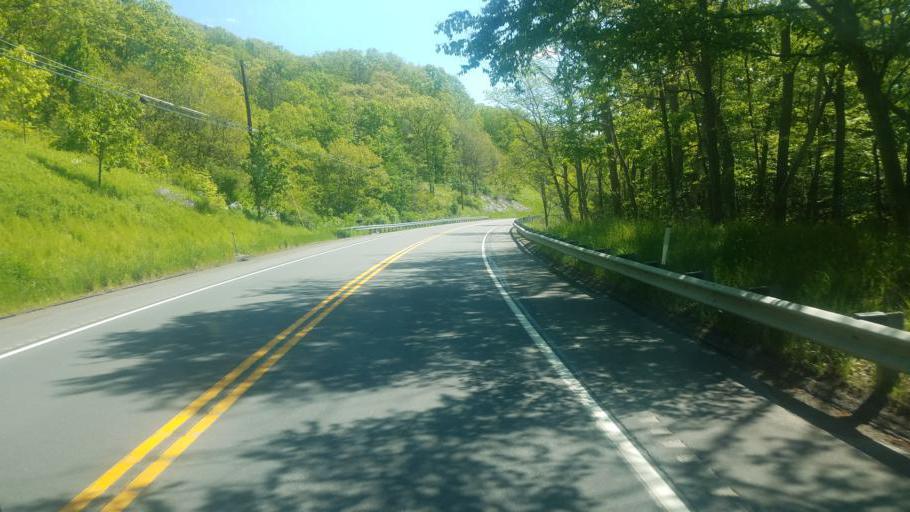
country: US
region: Pennsylvania
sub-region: Potter County
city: Galeton
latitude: 41.7546
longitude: -77.5282
